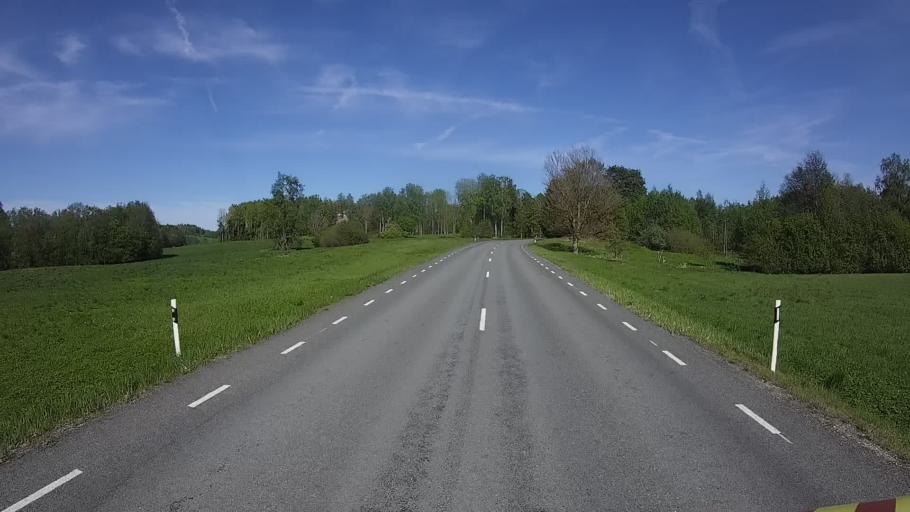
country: EE
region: Vorumaa
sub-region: Antsla vald
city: Vana-Antsla
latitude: 57.9504
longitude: 26.4266
